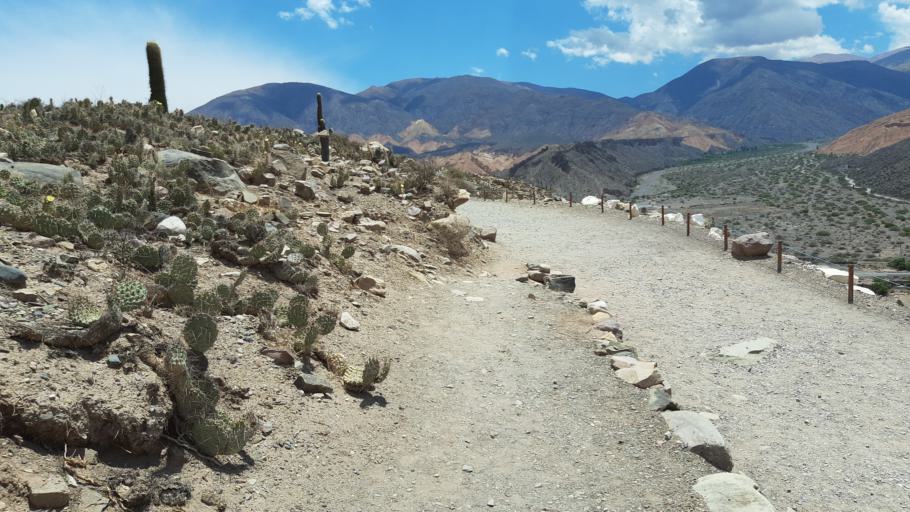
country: AR
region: Jujuy
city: Maimara
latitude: -23.5853
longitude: -65.4025
